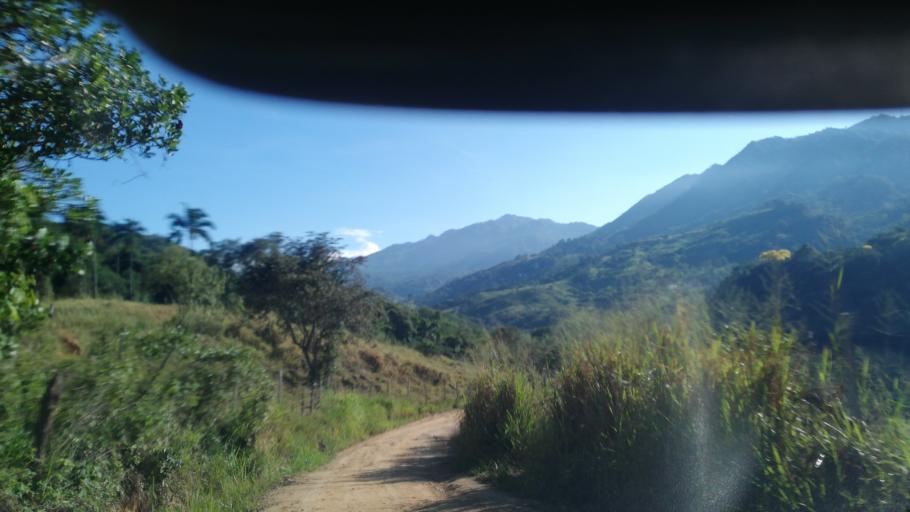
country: CO
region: Cundinamarca
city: Viani
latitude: 4.8356
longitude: -74.6190
